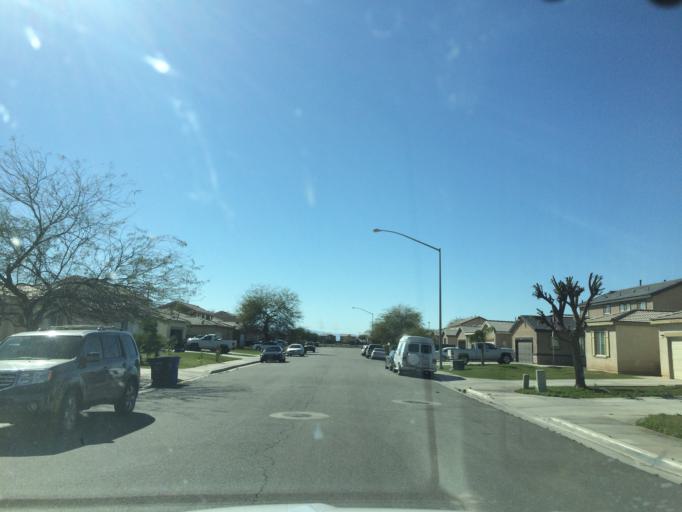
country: US
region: California
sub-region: Imperial County
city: Heber
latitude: 32.7363
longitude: -115.5373
